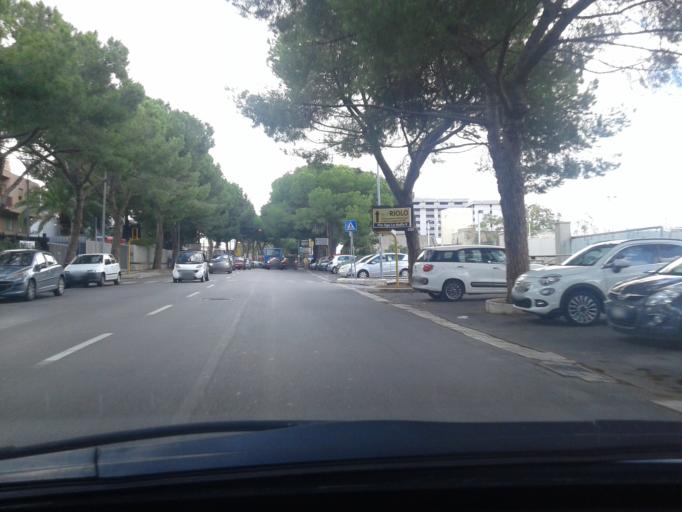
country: IT
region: Sicily
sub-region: Palermo
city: Palermo
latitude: 38.1554
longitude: 13.3197
